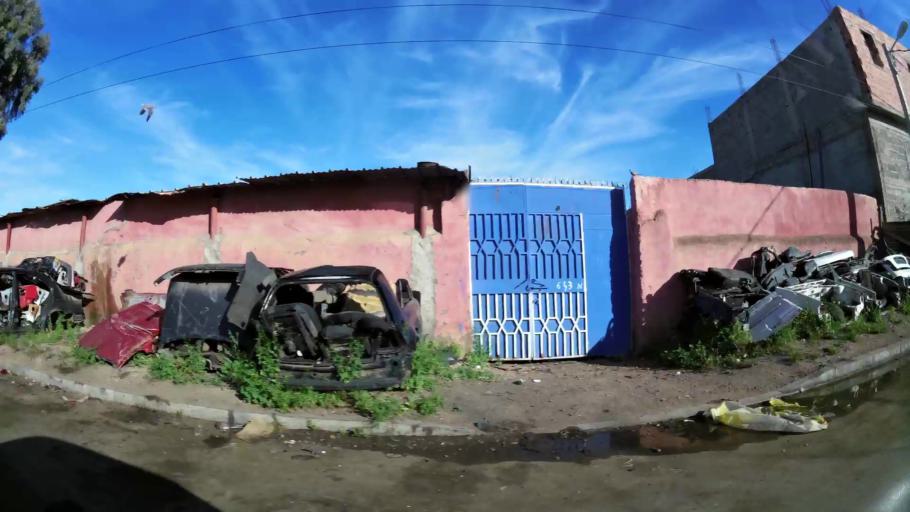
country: MA
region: Marrakech-Tensift-Al Haouz
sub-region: Marrakech
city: Marrakesh
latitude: 31.6849
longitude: -8.0555
